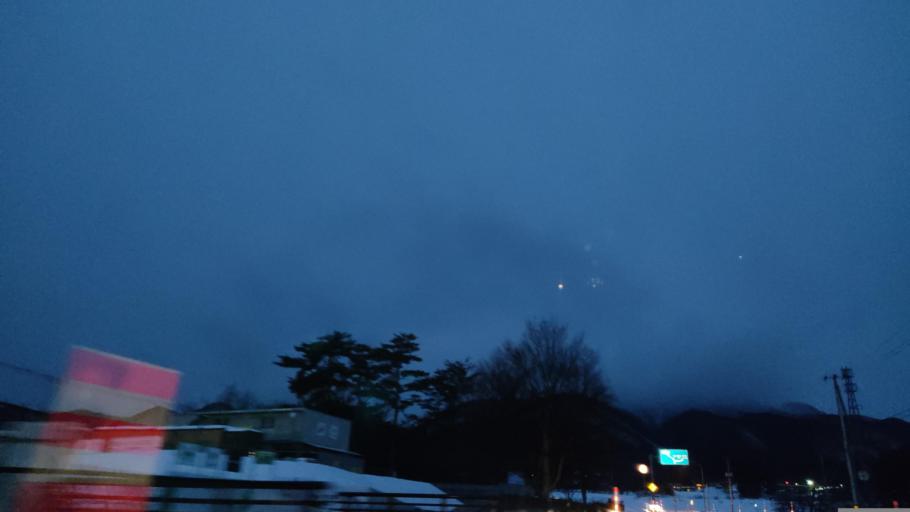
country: JP
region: Iwate
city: Morioka-shi
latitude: 39.6321
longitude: 141.0997
